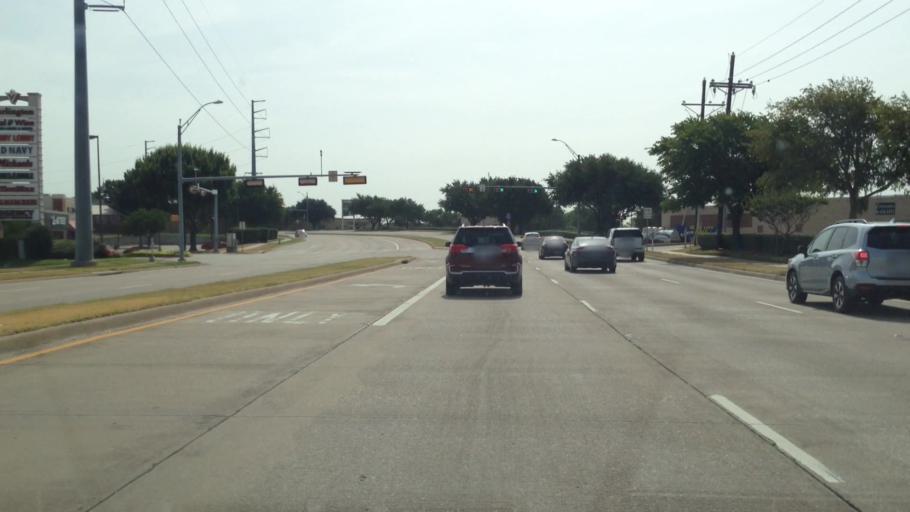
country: US
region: Texas
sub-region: Denton County
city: Lewisville
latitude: 33.0047
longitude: -96.9765
